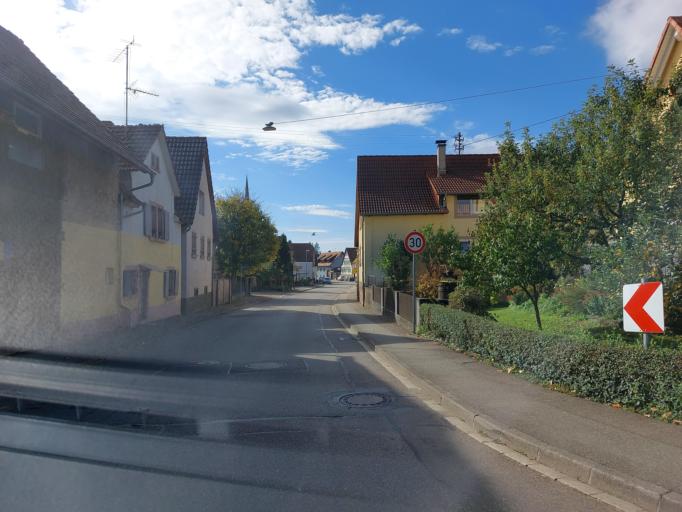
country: DE
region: Baden-Wuerttemberg
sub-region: Freiburg Region
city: Teningen
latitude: 48.1409
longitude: 7.8065
